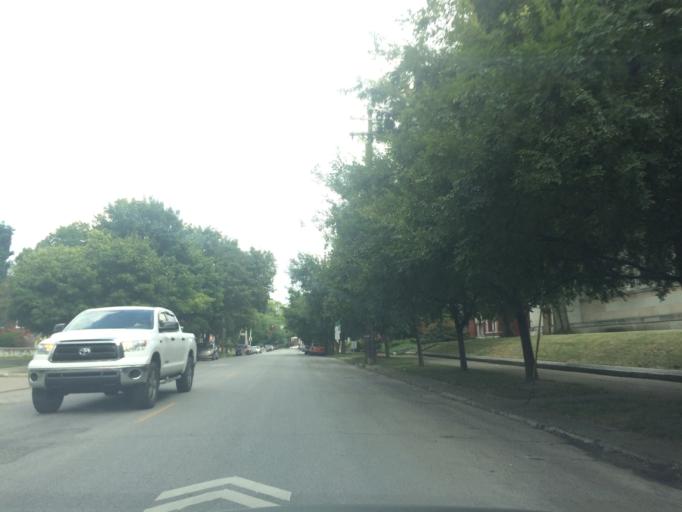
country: US
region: Kentucky
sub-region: Jefferson County
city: Louisville
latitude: 38.2327
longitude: -85.7590
